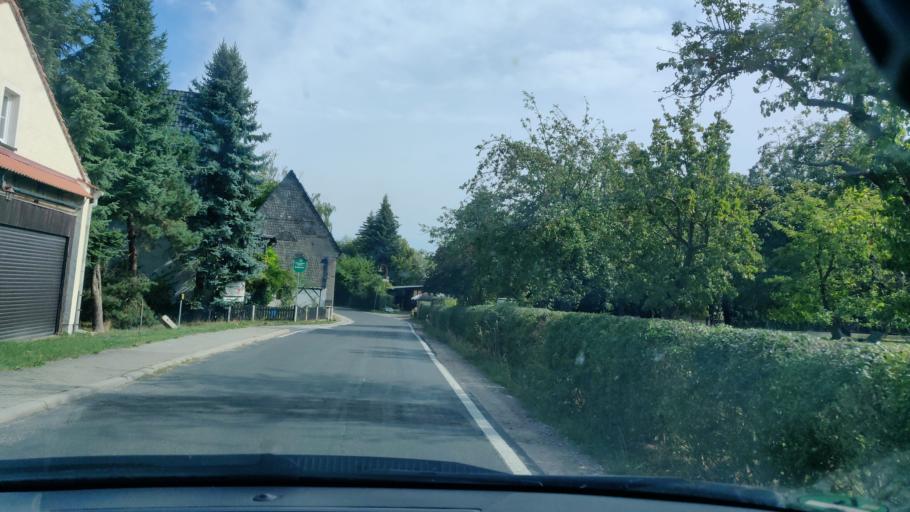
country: DE
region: Saxony
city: Konigsfeld
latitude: 51.0869
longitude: 12.7811
